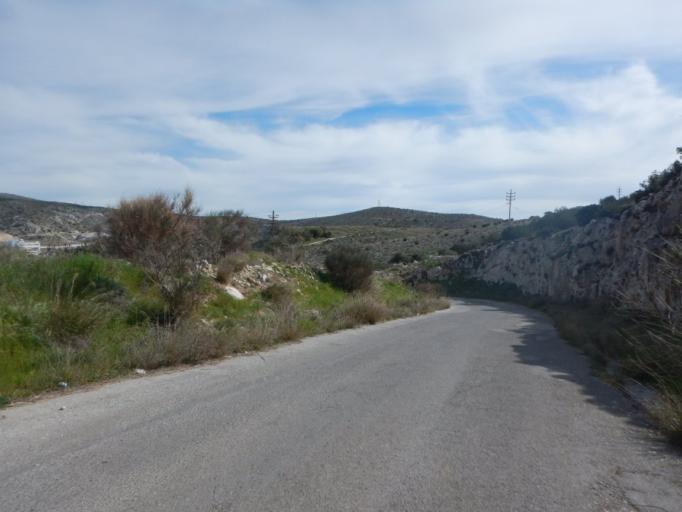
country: GR
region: Attica
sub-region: Nomos Piraios
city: Perama
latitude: 37.9763
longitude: 23.5932
